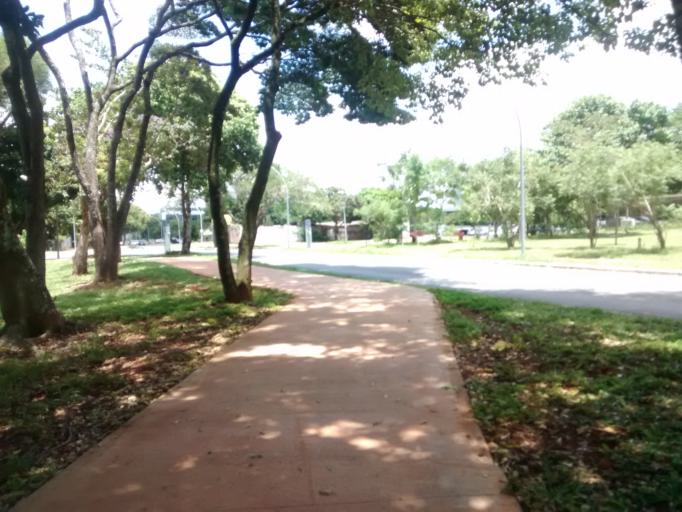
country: BR
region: Federal District
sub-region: Brasilia
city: Brasilia
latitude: -15.8108
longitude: -47.9085
